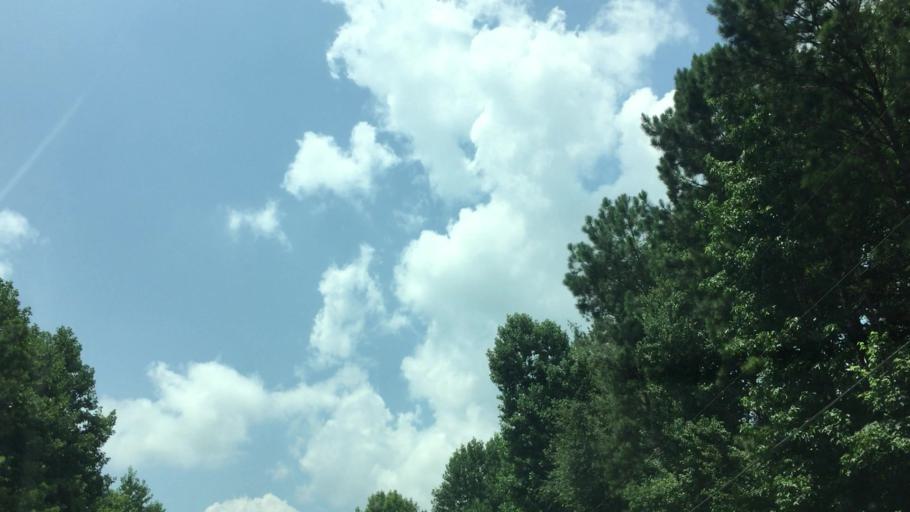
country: US
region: Georgia
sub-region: Carroll County
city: Villa Rica
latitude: 33.6176
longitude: -84.9512
